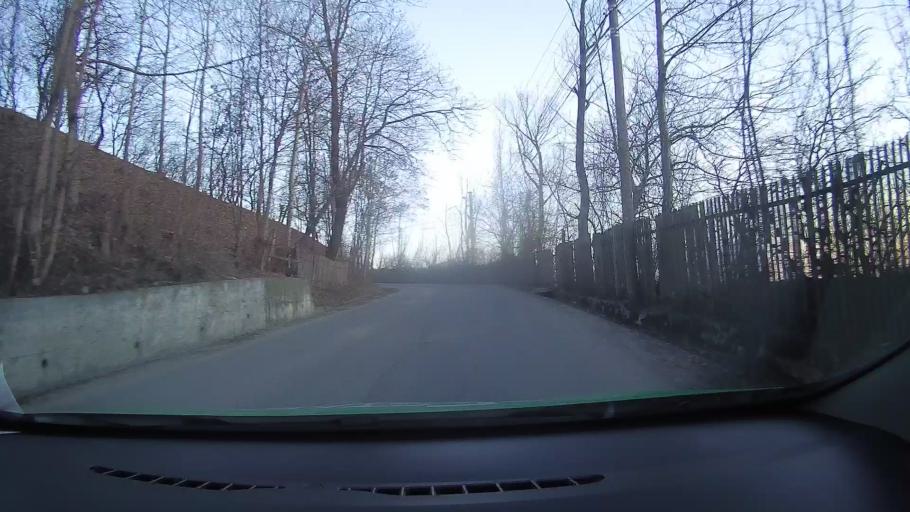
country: RO
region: Prahova
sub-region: Comuna Comarnic
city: Comarnic
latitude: 45.2490
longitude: 25.6422
